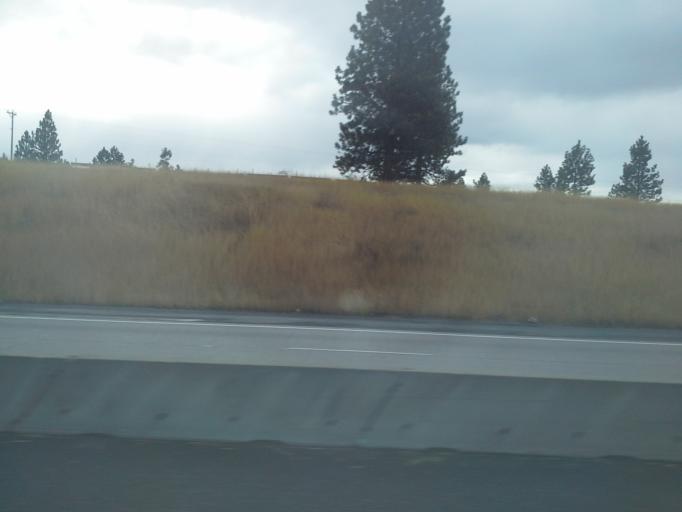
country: US
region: Oregon
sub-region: Umatilla County
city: Mission
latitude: 45.5871
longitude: -118.5678
